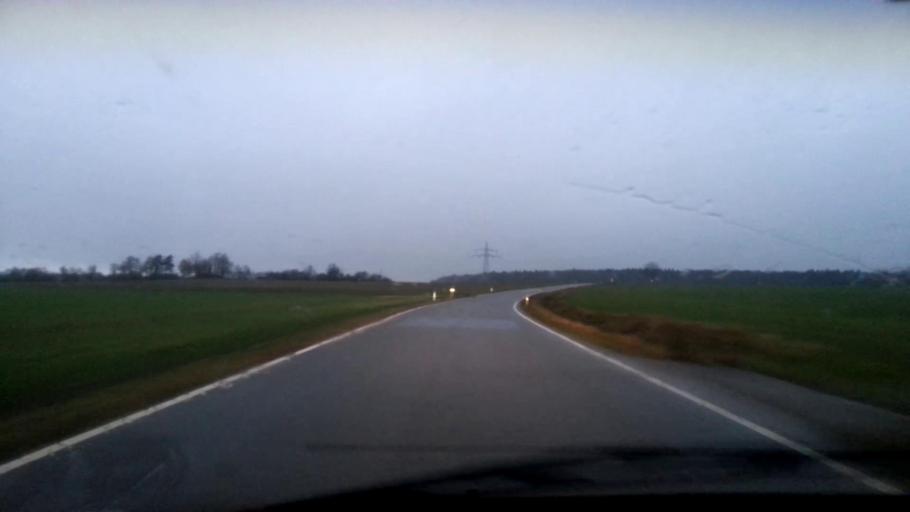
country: DE
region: Bavaria
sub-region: Upper Franconia
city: Konigsfeld
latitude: 49.9554
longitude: 11.1468
